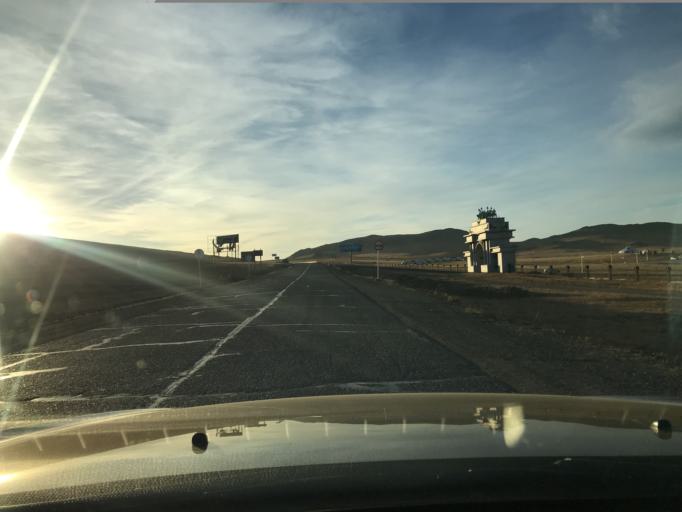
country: MN
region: Central Aimak
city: Arhust
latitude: 47.8044
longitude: 107.5342
